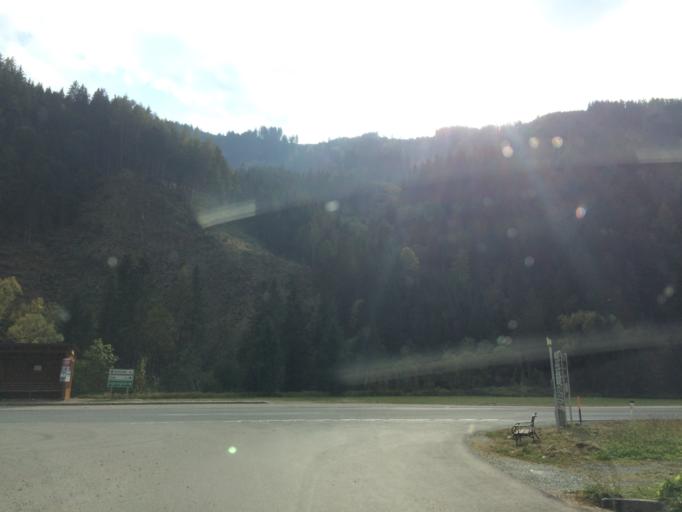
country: AT
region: Styria
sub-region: Politischer Bezirk Murtal
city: Seckau
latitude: 47.2558
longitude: 14.7482
